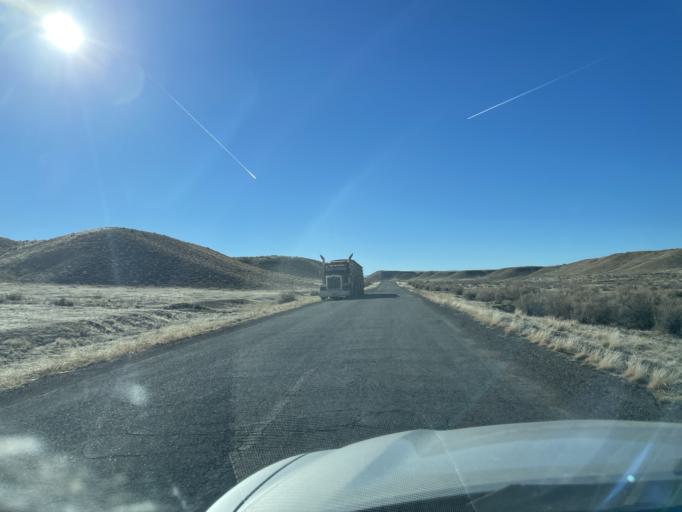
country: US
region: Colorado
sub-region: Mesa County
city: Loma
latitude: 39.2059
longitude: -109.1016
